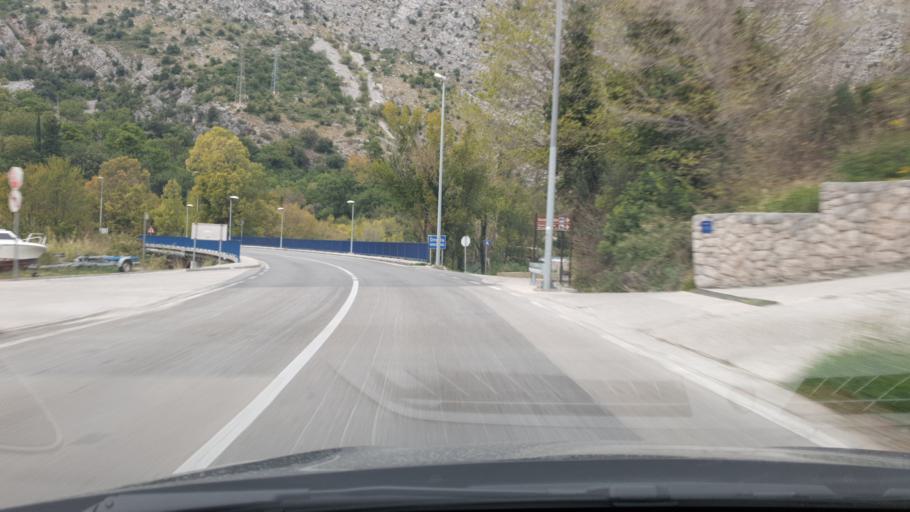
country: HR
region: Dubrovacko-Neretvanska
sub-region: Grad Dubrovnik
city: Mokosica
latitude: 42.6729
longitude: 18.1363
